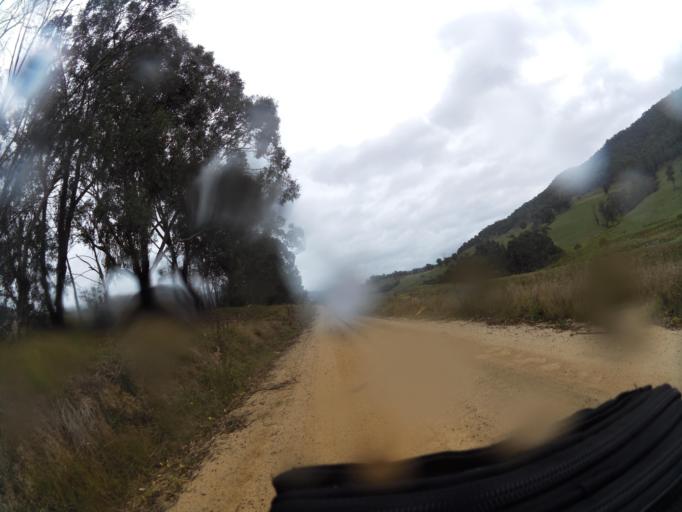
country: AU
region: New South Wales
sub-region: Greater Hume Shire
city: Holbrook
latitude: -36.2360
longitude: 147.6282
